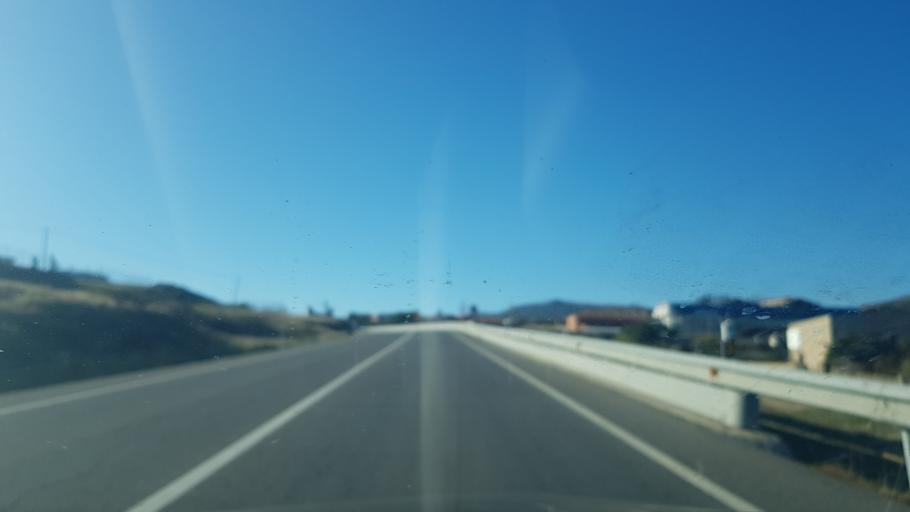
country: ES
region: Castille and Leon
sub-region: Provincia de Avila
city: Barraco
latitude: 40.4726
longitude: -4.6333
